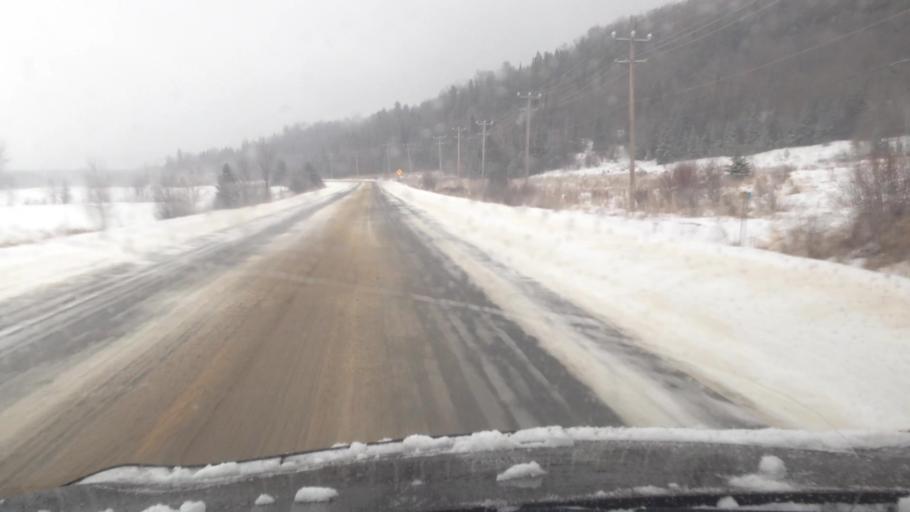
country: CA
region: Quebec
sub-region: Laurentides
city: Mont-Tremblant
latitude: 46.0645
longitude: -74.6213
